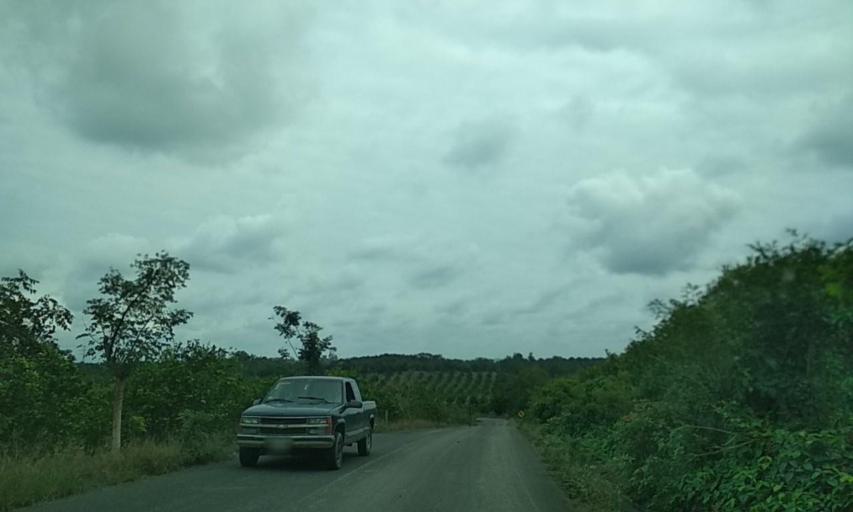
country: MX
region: Veracruz
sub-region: Papantla
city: El Chote
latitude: 20.3500
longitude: -97.3822
